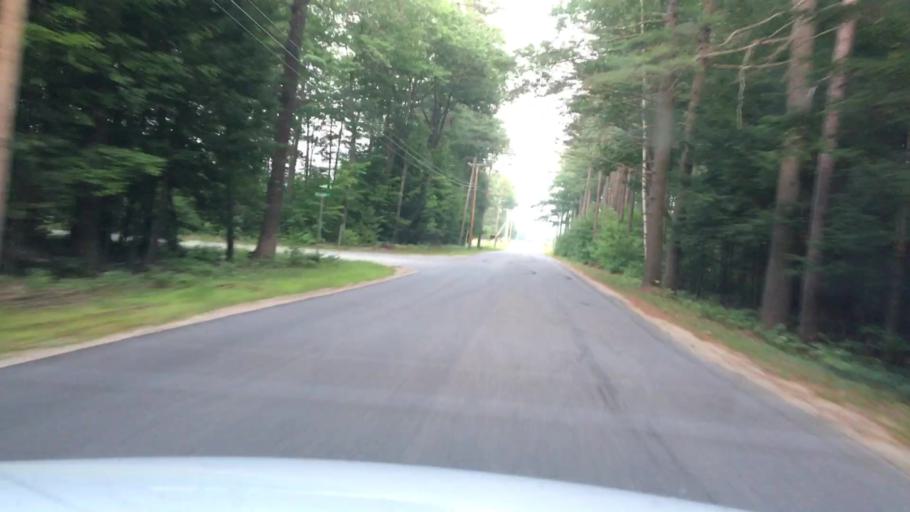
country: US
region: Maine
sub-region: Oxford County
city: Bethel
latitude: 44.4209
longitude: -70.8110
